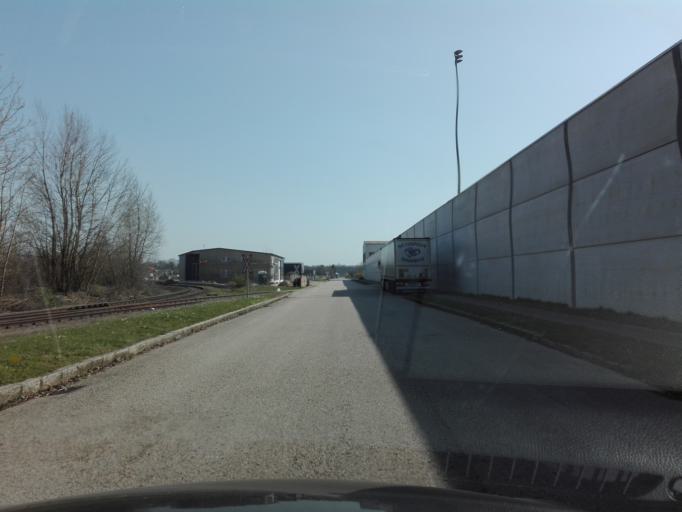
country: AT
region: Lower Austria
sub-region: Politischer Bezirk Amstetten
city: Ennsdorf
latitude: 48.2271
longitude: 14.5075
